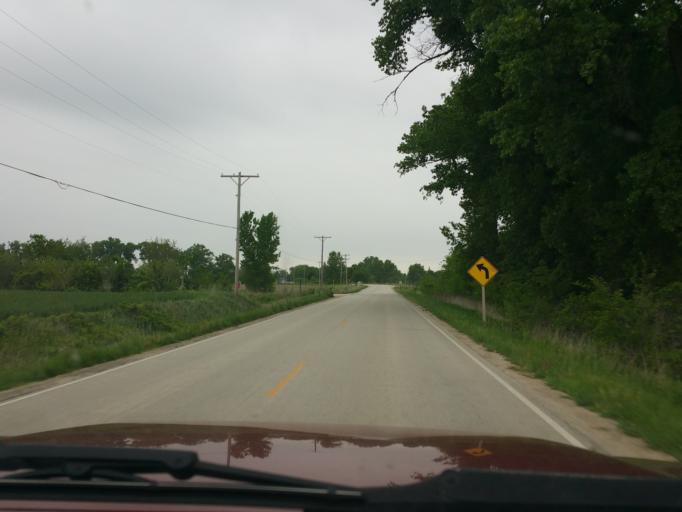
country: US
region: Kansas
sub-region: Riley County
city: Manhattan
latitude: 39.2426
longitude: -96.5712
